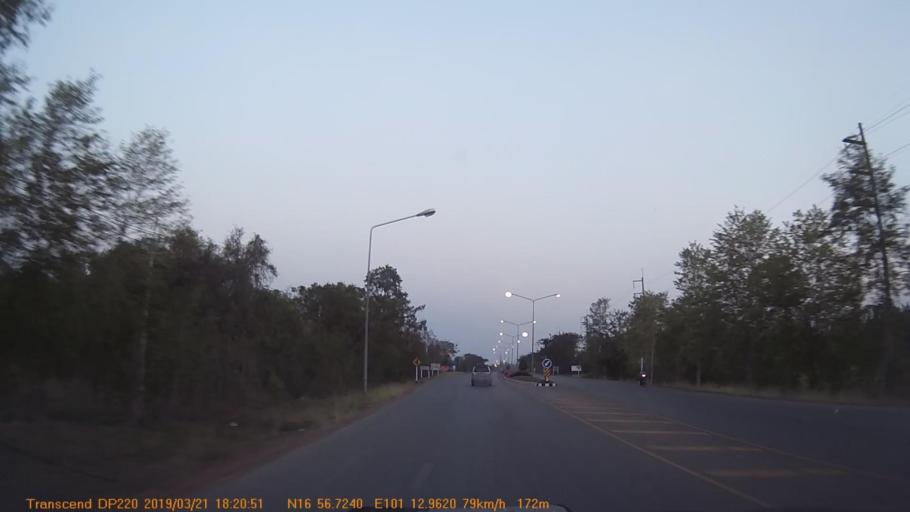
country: TH
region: Phetchabun
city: Lom Kao
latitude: 16.9450
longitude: 101.2162
